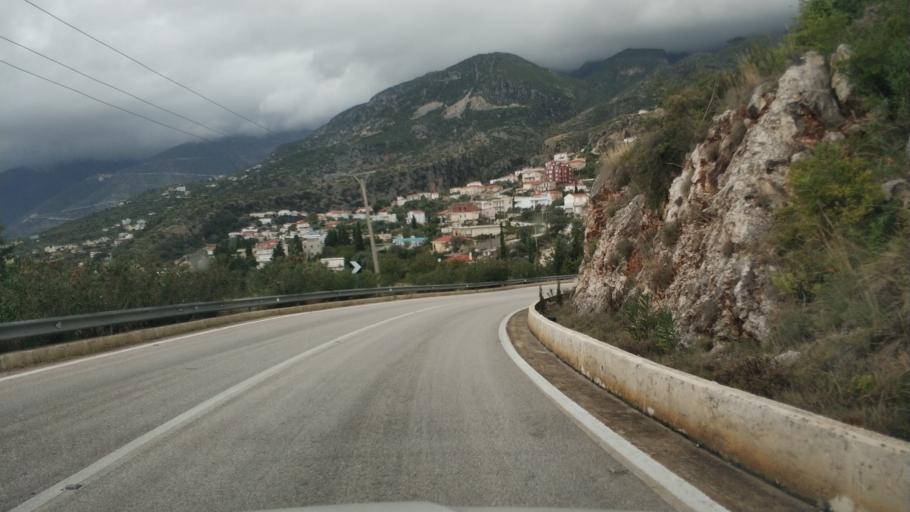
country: AL
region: Vlore
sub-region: Rrethi i Vlores
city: Vranisht
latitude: 40.1465
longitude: 19.6432
